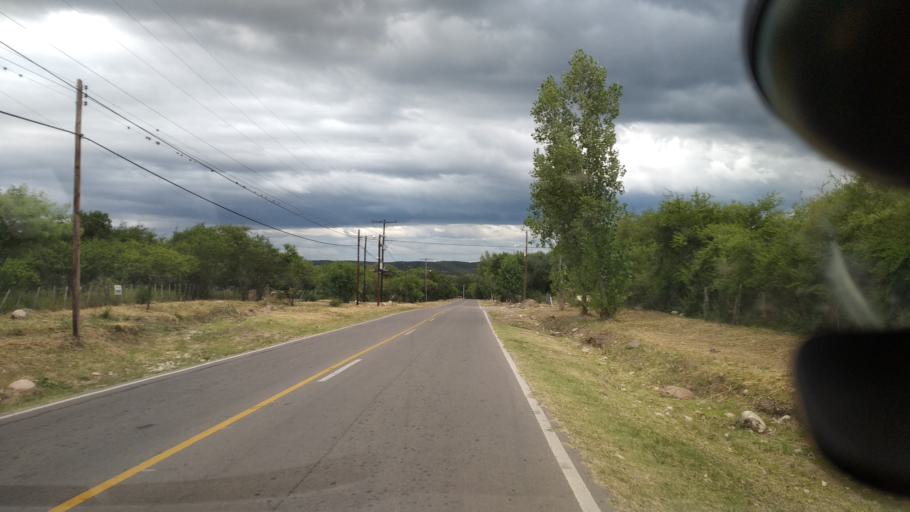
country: AR
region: Cordoba
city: Villa Las Rosas
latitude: -31.9383
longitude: -65.0372
